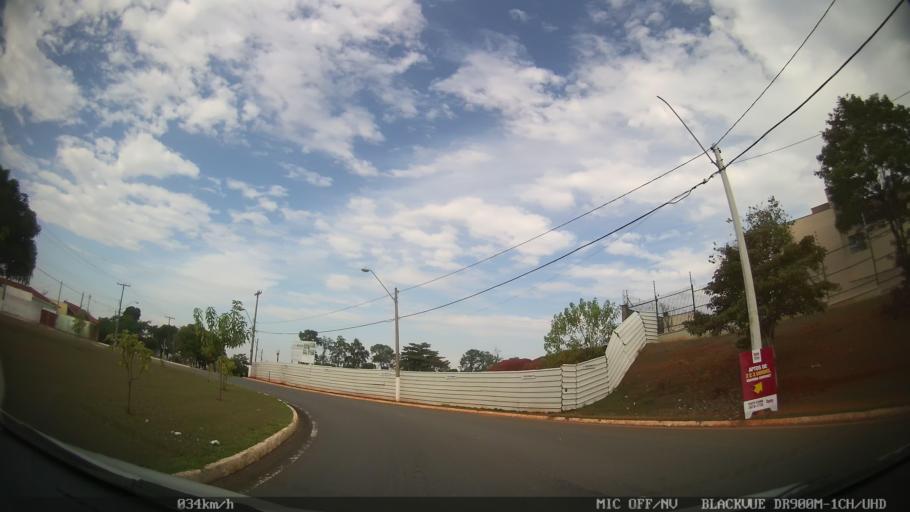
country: BR
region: Sao Paulo
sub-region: Paulinia
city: Paulinia
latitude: -22.7523
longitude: -47.1733
